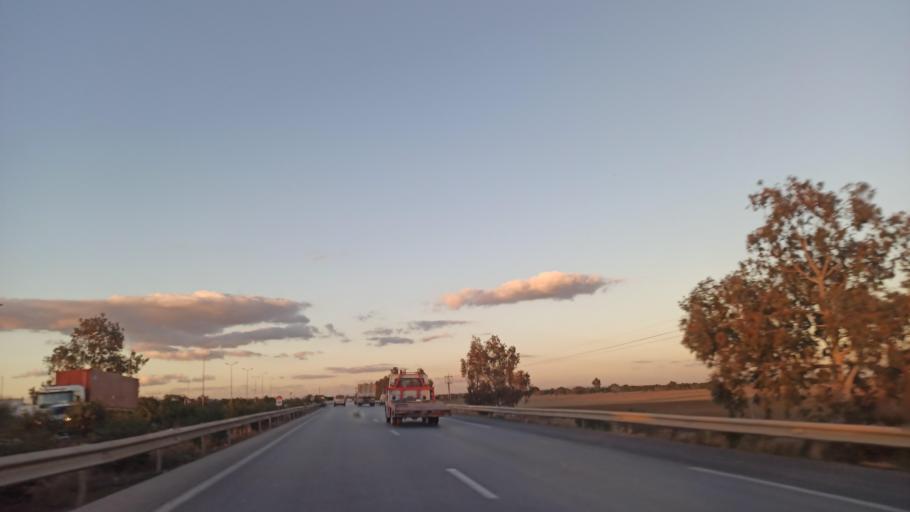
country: TN
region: Susah
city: Harqalah
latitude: 36.1292
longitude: 10.4068
